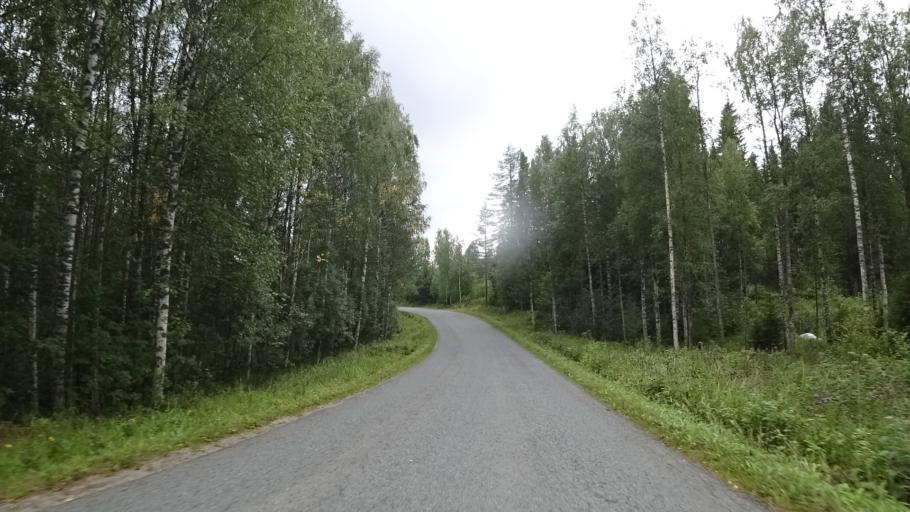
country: FI
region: North Karelia
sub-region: Joensuu
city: Ilomantsi
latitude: 62.9508
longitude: 31.2954
